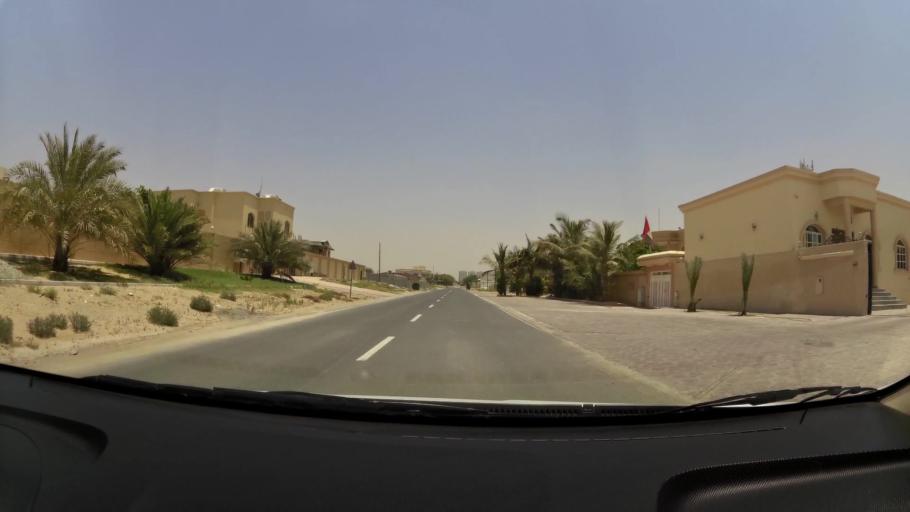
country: AE
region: Ajman
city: Ajman
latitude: 25.4126
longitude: 55.4928
